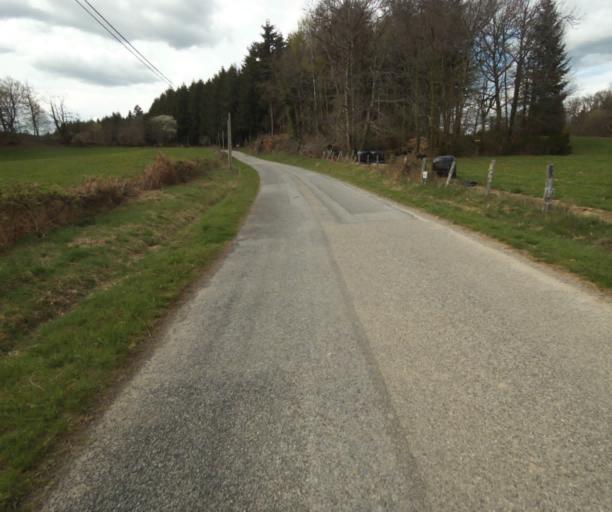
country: FR
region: Limousin
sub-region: Departement de la Correze
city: Argentat
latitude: 45.1881
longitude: 1.9345
